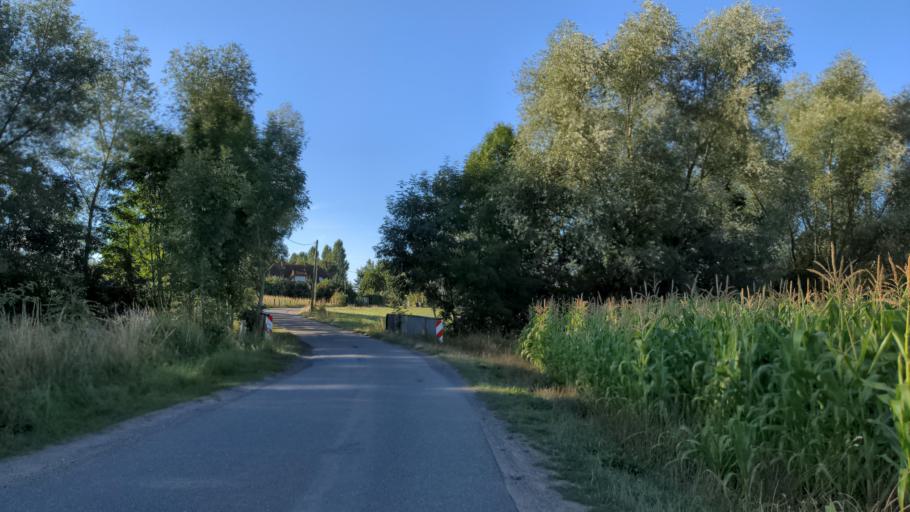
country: DE
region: Mecklenburg-Vorpommern
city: Kalkhorst
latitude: 53.9593
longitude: 11.0079
